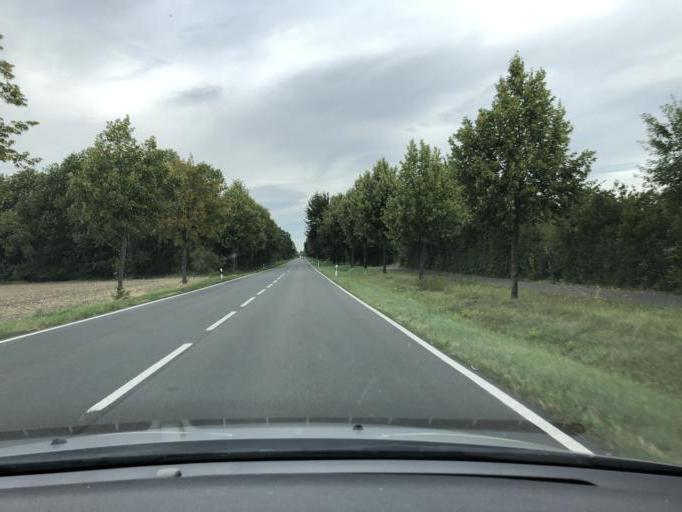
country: DE
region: Saxony
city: Zschortau
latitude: 51.4602
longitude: 12.3677
